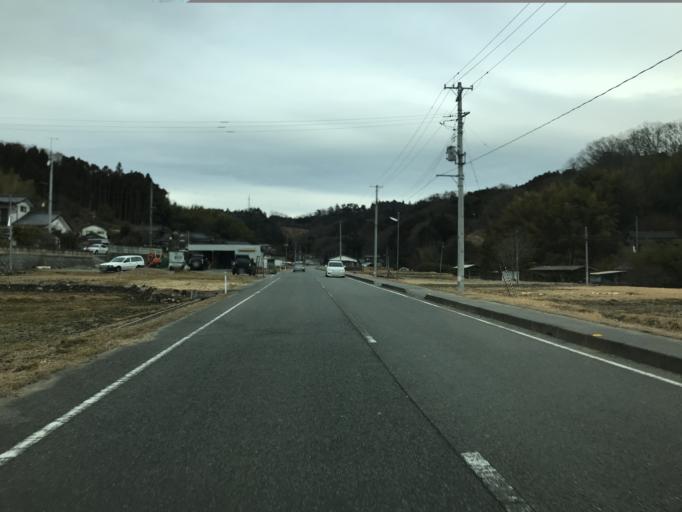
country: JP
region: Fukushima
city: Iwaki
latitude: 37.0755
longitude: 140.9037
